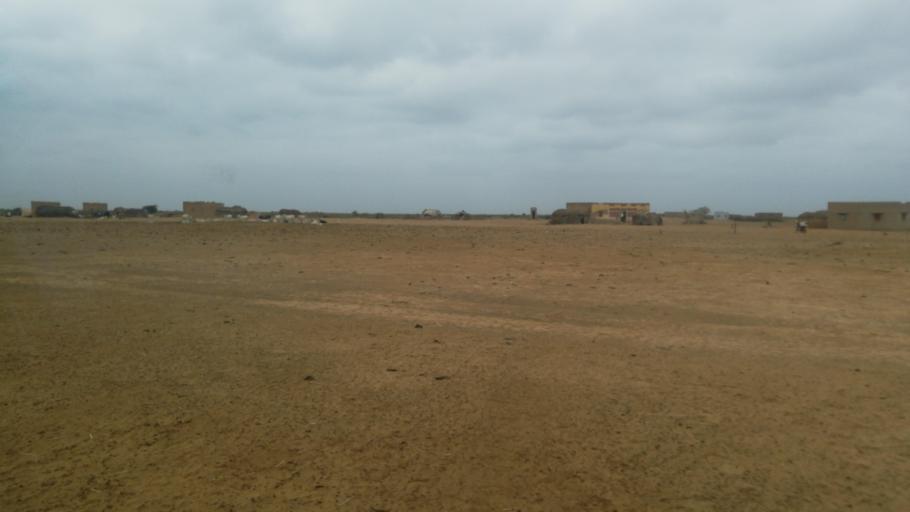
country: SN
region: Saint-Louis
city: Saint-Louis
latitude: 16.3135
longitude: -16.2274
